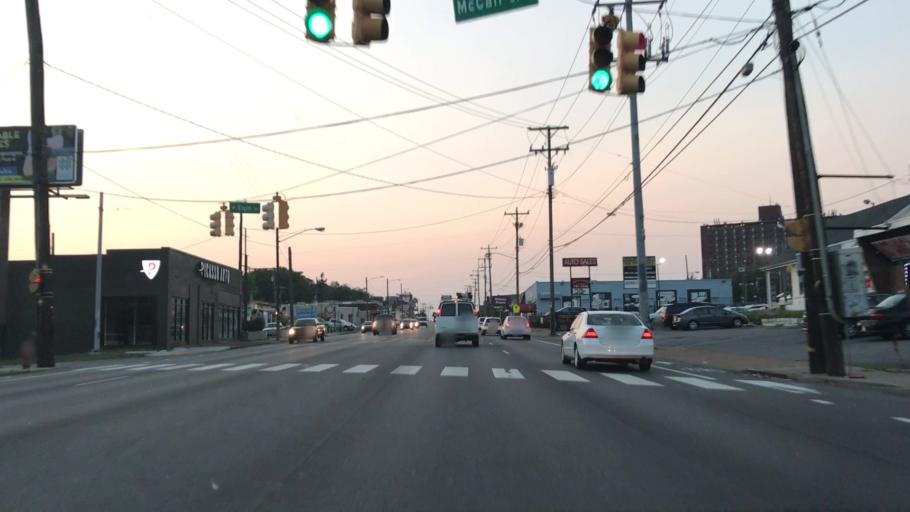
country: US
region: Tennessee
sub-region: Davidson County
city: Oak Hill
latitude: 36.0996
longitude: -86.7394
